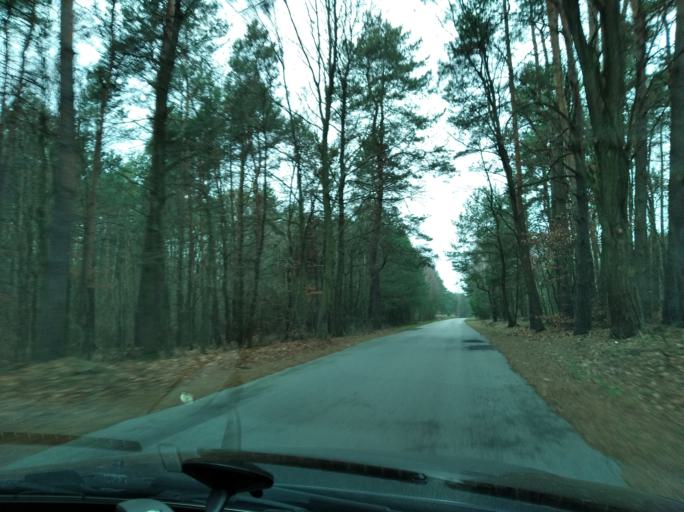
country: PL
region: Subcarpathian Voivodeship
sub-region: Powiat lancucki
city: Brzoza Stadnicka
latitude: 50.2040
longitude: 22.2765
